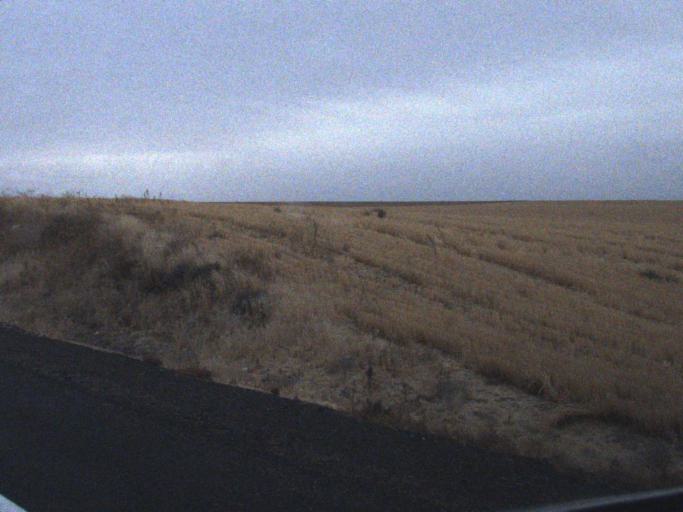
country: US
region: Washington
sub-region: Franklin County
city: Connell
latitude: 46.7944
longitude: -118.7102
